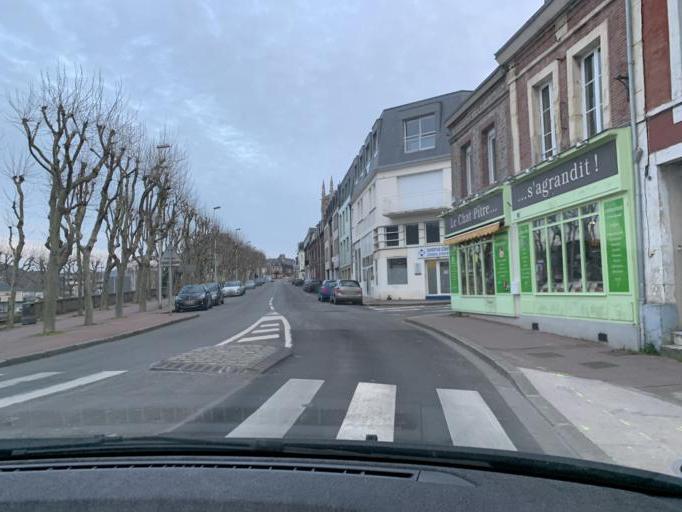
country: FR
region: Haute-Normandie
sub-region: Departement de la Seine-Maritime
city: Fecamp
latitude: 49.7592
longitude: 0.3732
